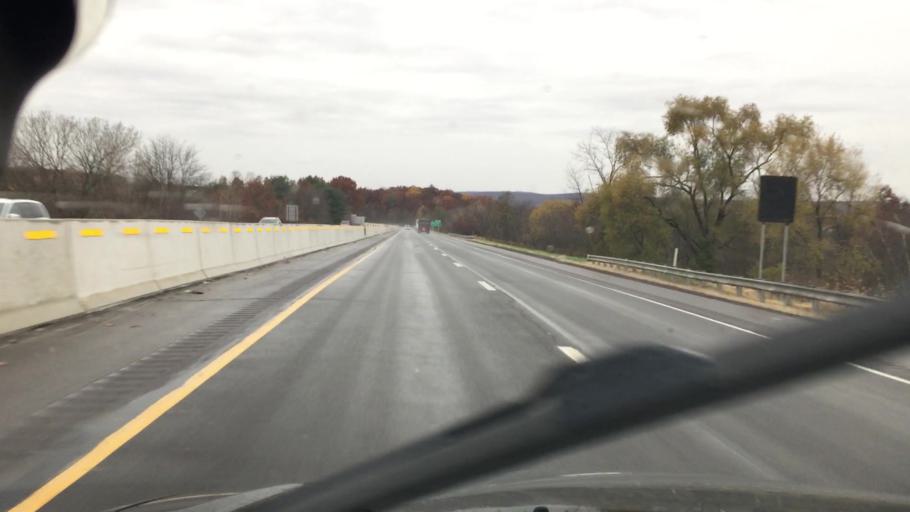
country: US
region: Pennsylvania
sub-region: Luzerne County
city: Ashley
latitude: 41.2011
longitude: -75.9262
